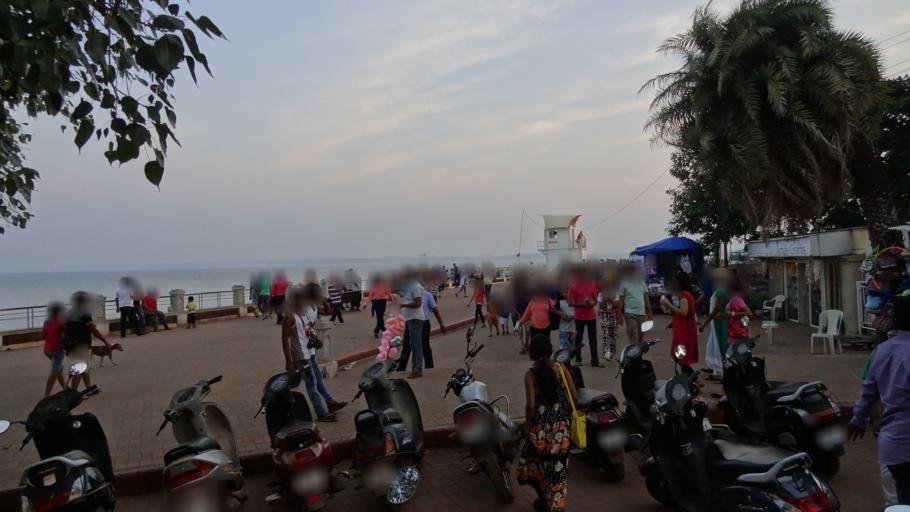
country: IN
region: Goa
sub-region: North Goa
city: Taleigao
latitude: 15.4520
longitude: 73.8032
